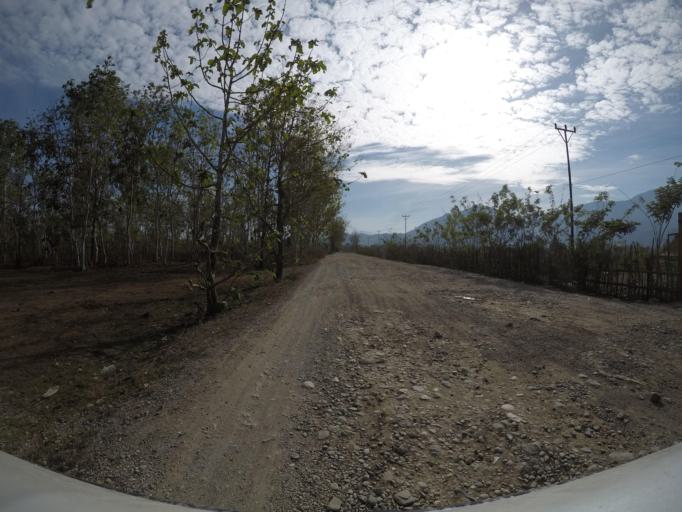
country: TL
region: Bobonaro
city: Maliana
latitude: -8.9308
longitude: 125.2002
